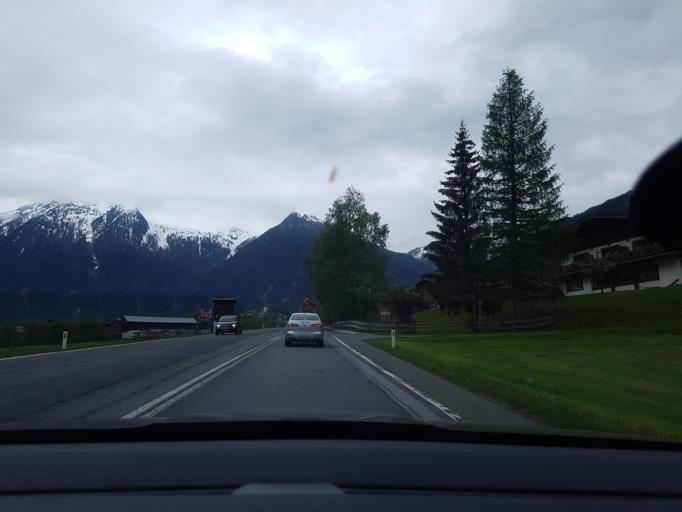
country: AT
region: Salzburg
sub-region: Politischer Bezirk Zell am See
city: Krimml
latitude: 47.2283
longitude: 12.1847
